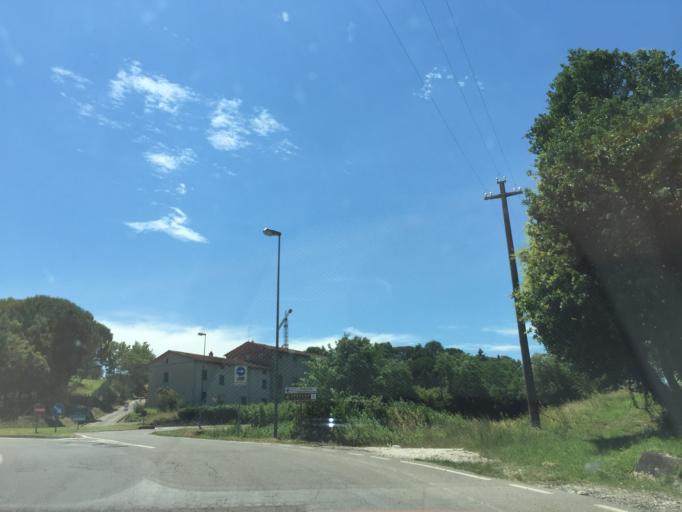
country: IT
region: Tuscany
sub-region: Province of Pisa
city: San Miniato
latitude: 43.6879
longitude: 10.7835
